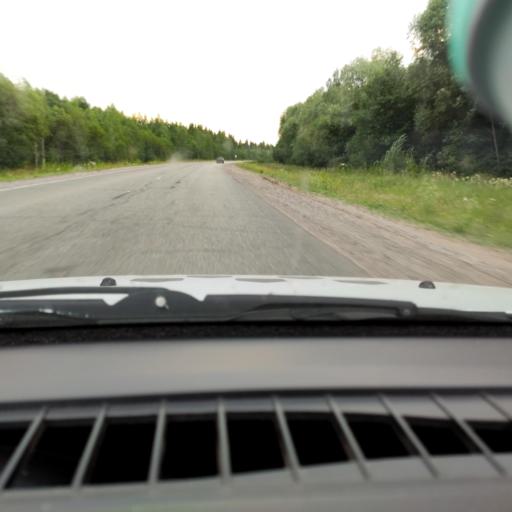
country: RU
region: Udmurtiya
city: Debesy
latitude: 57.6040
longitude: 53.4618
